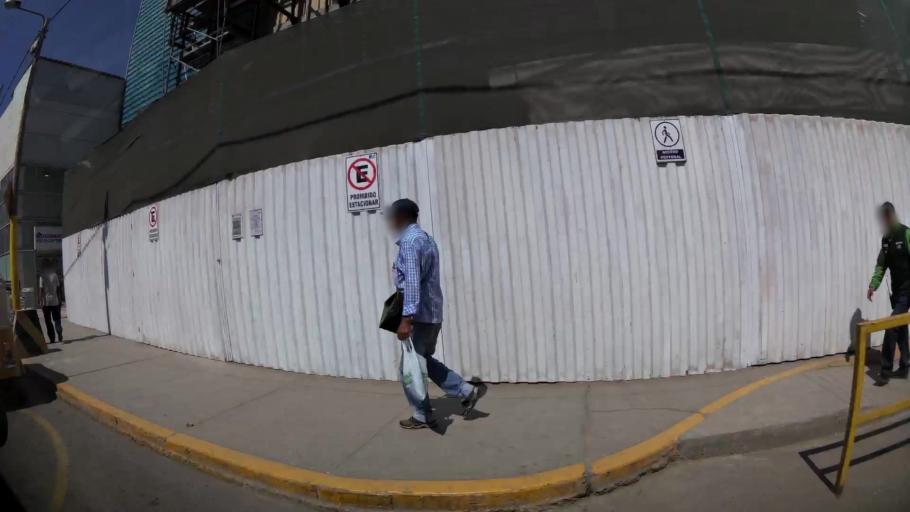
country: PE
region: Ica
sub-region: Provincia de Ica
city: Ica
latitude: -14.0705
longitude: -75.7286
